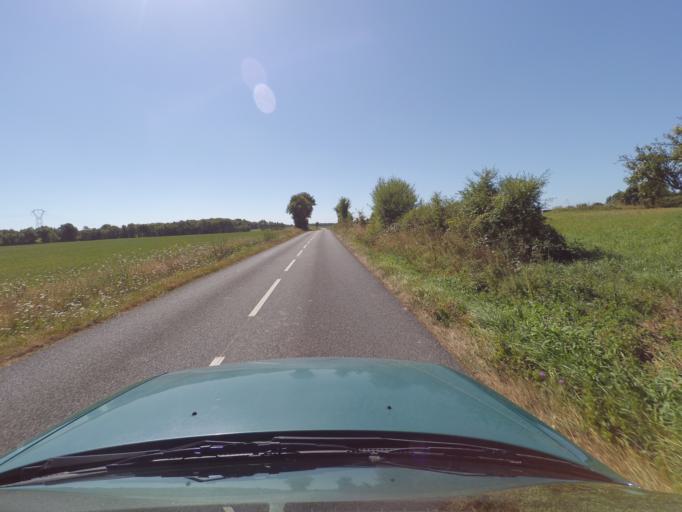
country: FR
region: Pays de la Loire
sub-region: Departement de la Loire-Atlantique
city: Le Bignon
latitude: 47.1144
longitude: -1.5017
